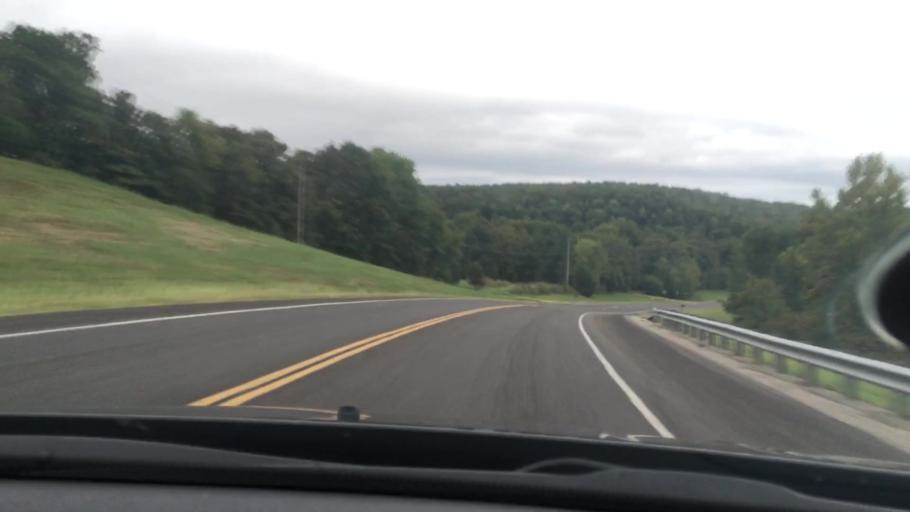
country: US
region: Oklahoma
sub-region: Sequoyah County
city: Vian
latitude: 35.5424
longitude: -94.9684
